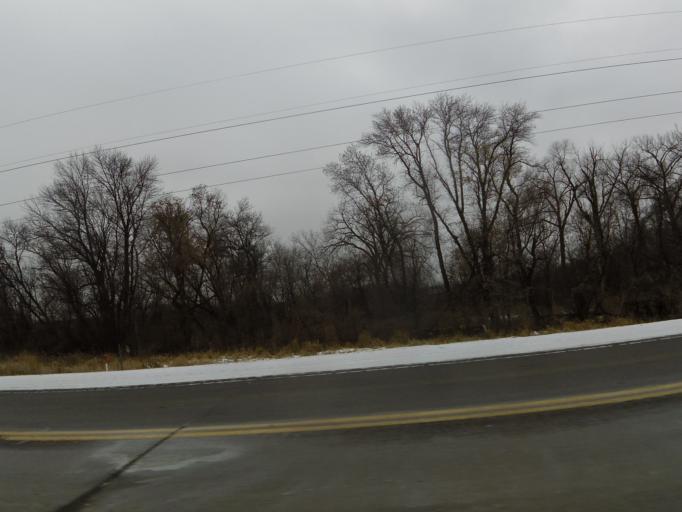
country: US
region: Minnesota
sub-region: Wright County
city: Delano
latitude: 45.0529
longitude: -93.8019
